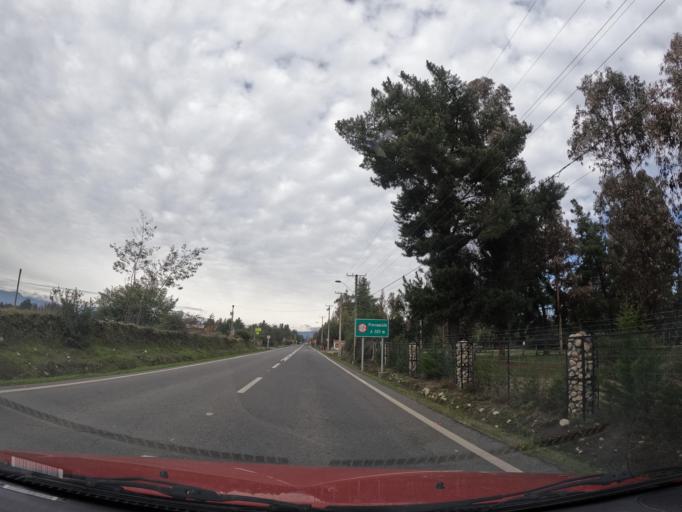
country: CL
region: Maule
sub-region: Provincia de Linares
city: Linares
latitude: -35.8931
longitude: -71.5238
